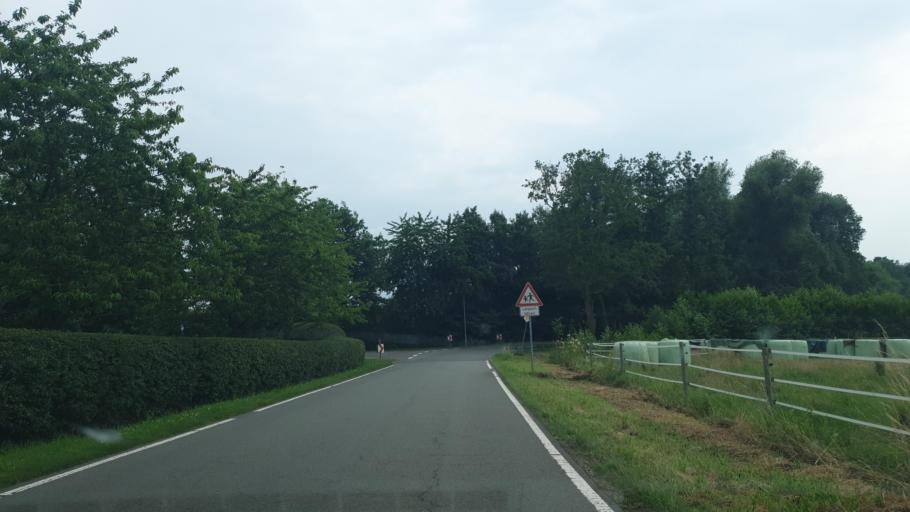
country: DE
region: North Rhine-Westphalia
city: Bad Oeynhausen
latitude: 52.2391
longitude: 8.7961
